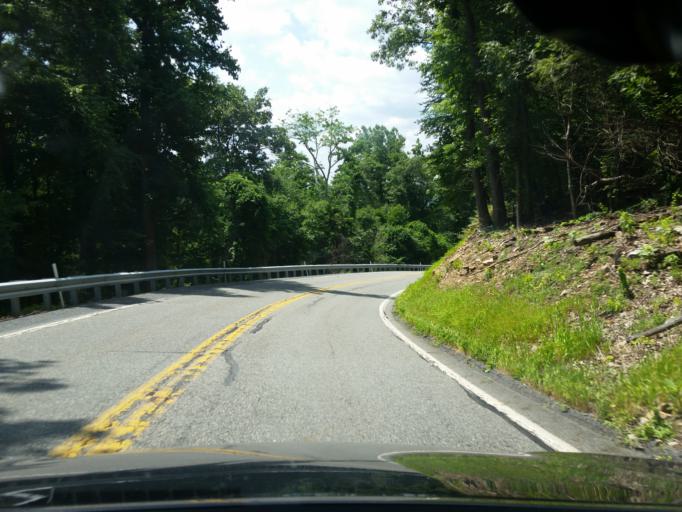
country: US
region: Pennsylvania
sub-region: Dauphin County
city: Matamoras
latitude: 40.4089
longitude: -76.9340
